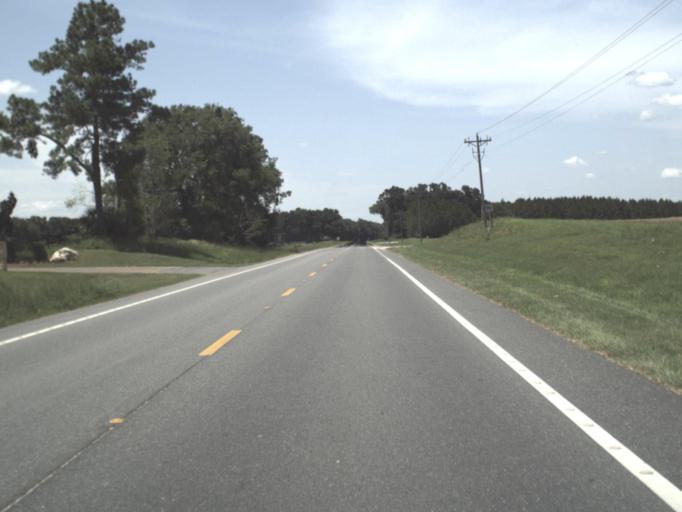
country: US
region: Florida
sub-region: Gilchrist County
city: Trenton
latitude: 29.8274
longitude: -82.8673
